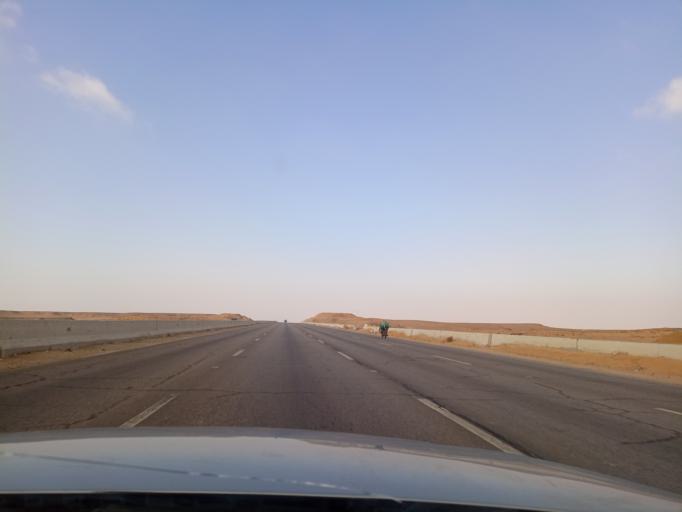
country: EG
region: Al Jizah
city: Al `Ayyat
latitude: 29.6666
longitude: 31.1788
